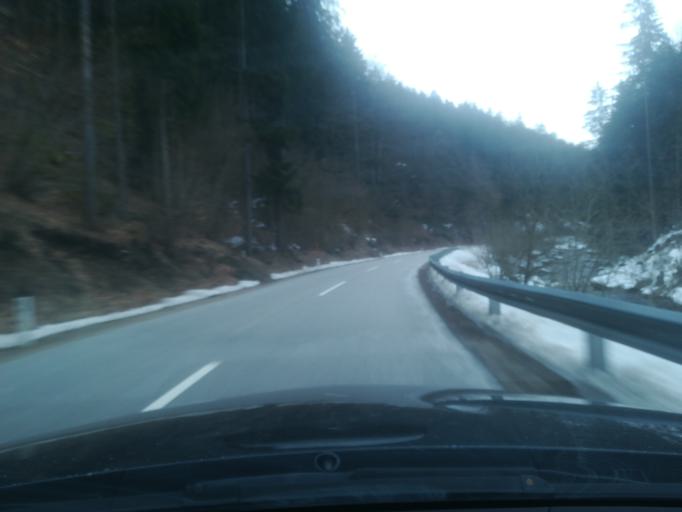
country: AT
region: Upper Austria
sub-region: Politischer Bezirk Perg
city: Perg
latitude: 48.4017
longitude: 14.6352
